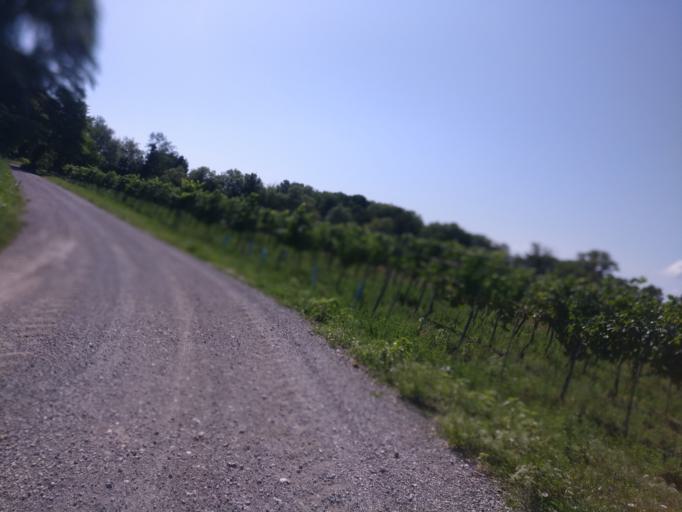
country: AT
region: Lower Austria
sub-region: Politischer Bezirk Baden
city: Pottendorf
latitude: 47.9112
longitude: 16.3532
